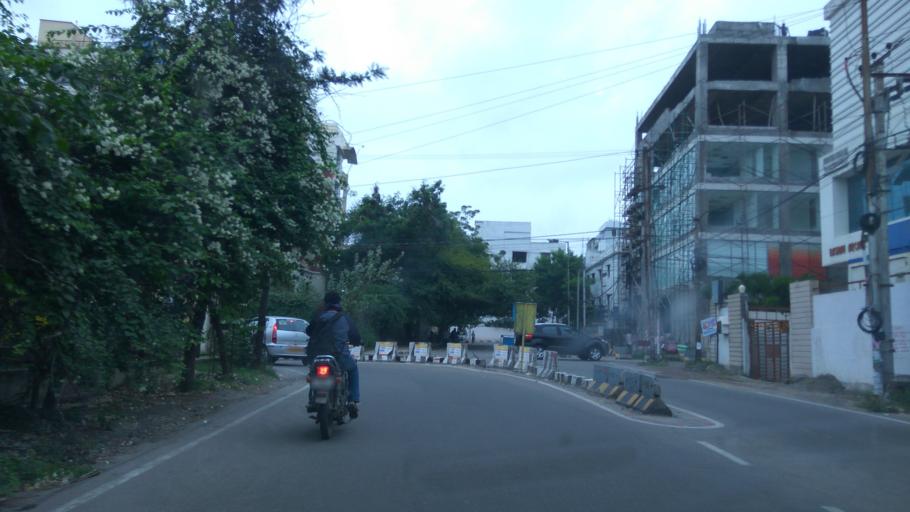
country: IN
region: Telangana
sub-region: Rangareddi
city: Kukatpalli
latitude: 17.4374
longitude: 78.3931
